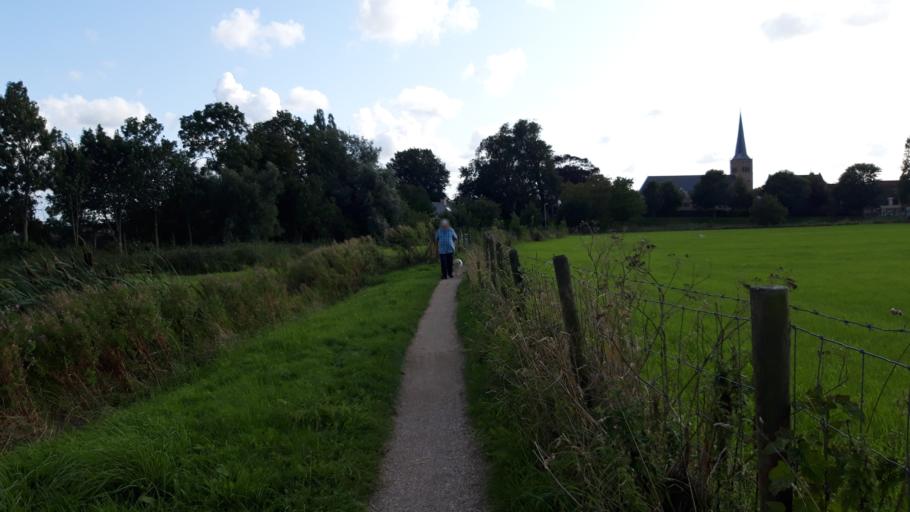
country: NL
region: Friesland
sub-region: Gemeente Franekeradeel
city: Franeker
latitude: 53.1894
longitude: 5.5482
